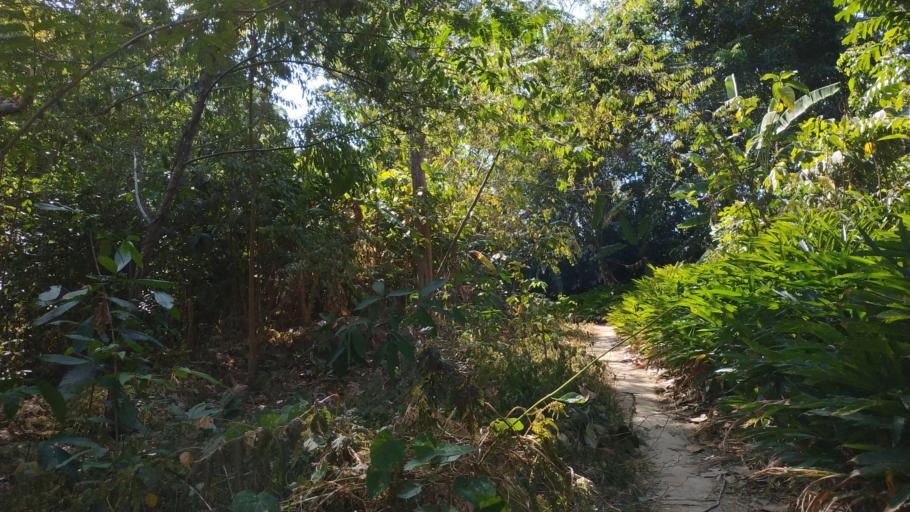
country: TH
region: Phuket
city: Patong
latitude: 7.8740
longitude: 98.2771
